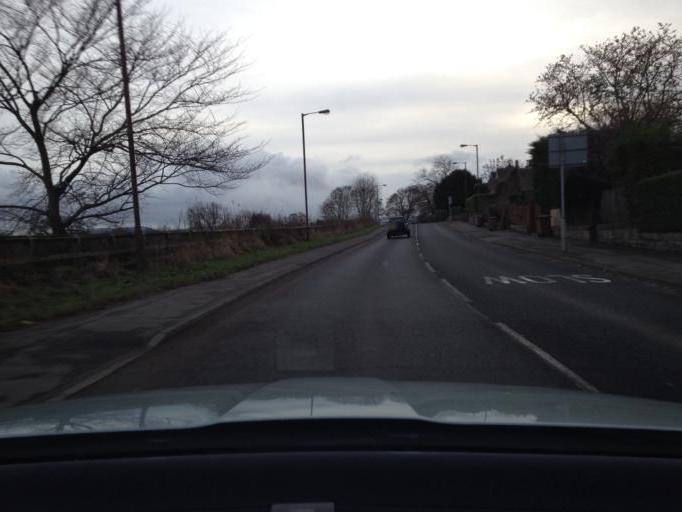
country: GB
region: Scotland
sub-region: Edinburgh
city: Kirkliston
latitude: 55.9519
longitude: -3.4046
